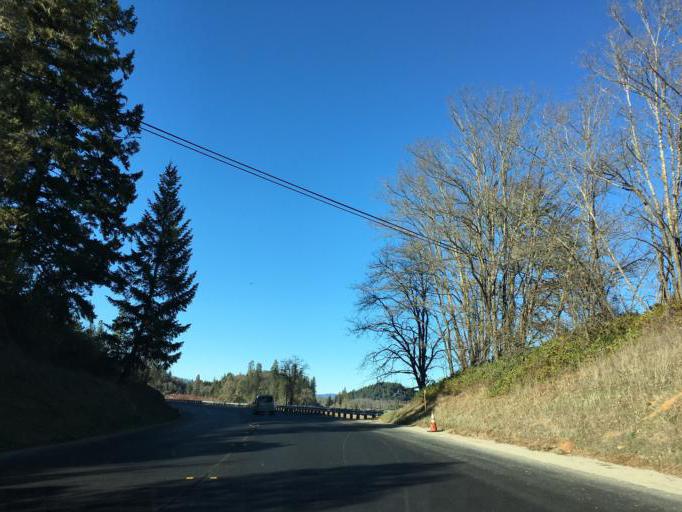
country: US
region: California
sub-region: Mendocino County
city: Laytonville
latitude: 39.6304
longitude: -123.4630
